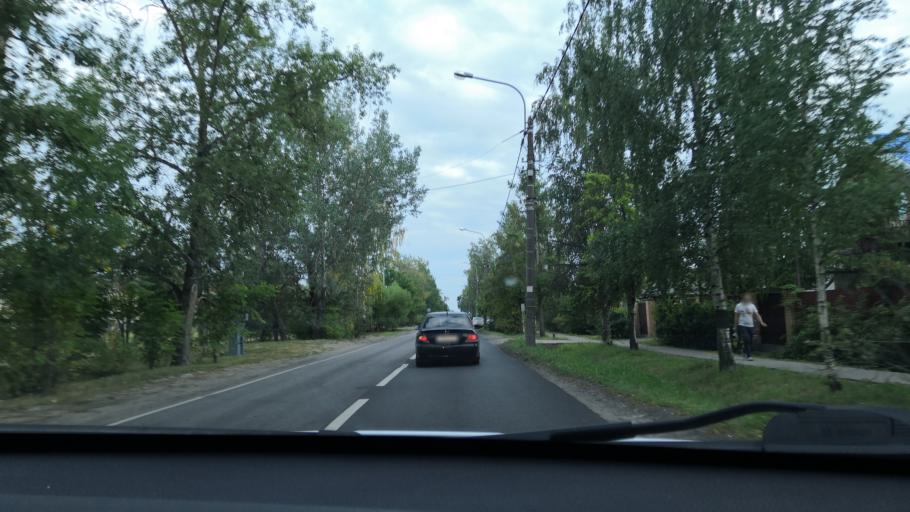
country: RU
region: St.-Petersburg
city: Pushkin
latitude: 59.6987
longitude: 30.4103
